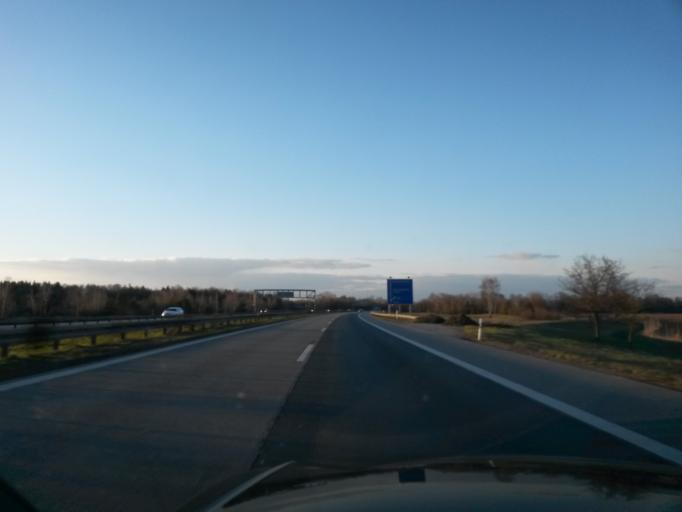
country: DE
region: Bavaria
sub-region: Upper Bavaria
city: Oberschleissheim
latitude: 48.2455
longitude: 11.5337
